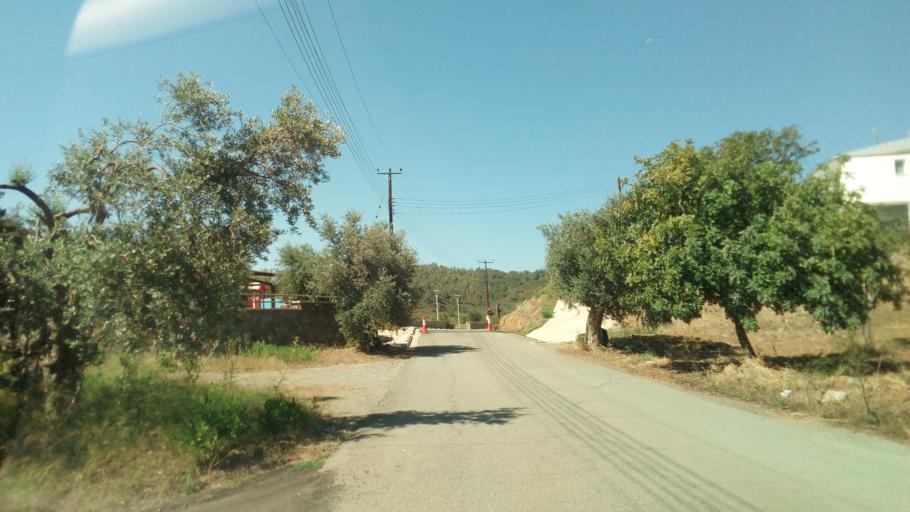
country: CY
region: Limassol
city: Parekklisha
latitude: 34.8656
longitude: 33.1553
